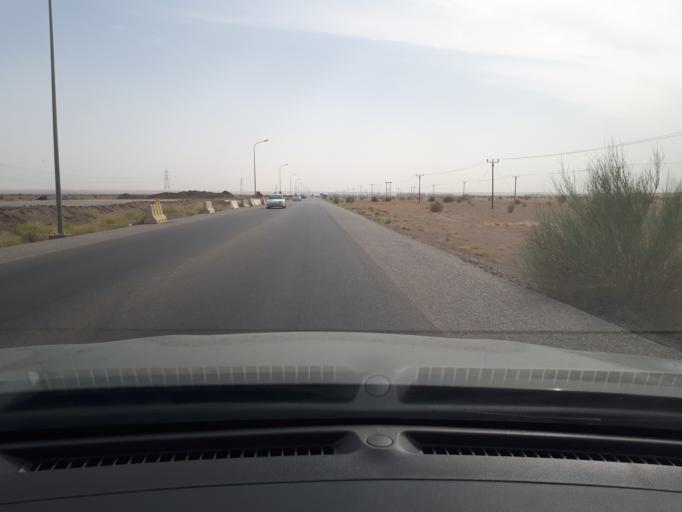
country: OM
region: Ash Sharqiyah
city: Badiyah
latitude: 22.4739
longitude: 58.9020
